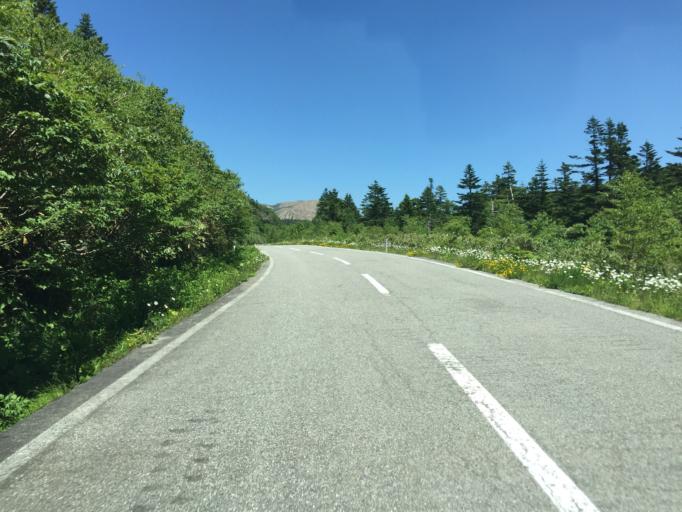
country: JP
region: Fukushima
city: Inawashiro
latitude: 37.6981
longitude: 140.2481
